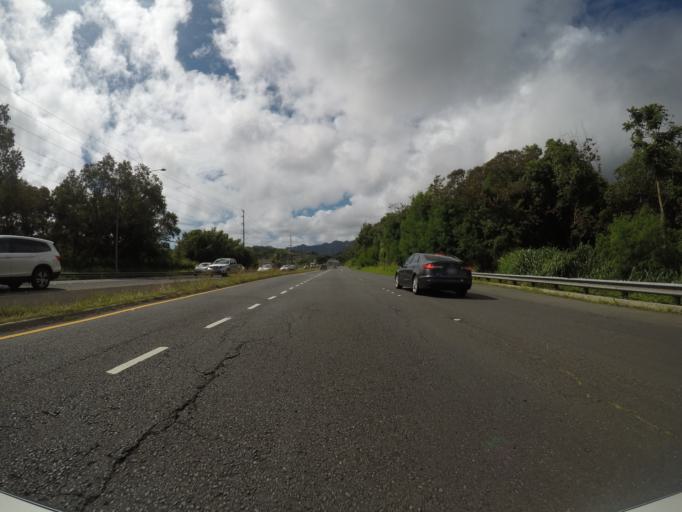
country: US
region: Hawaii
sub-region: Honolulu County
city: Waimanalo
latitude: 21.3688
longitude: -157.7408
